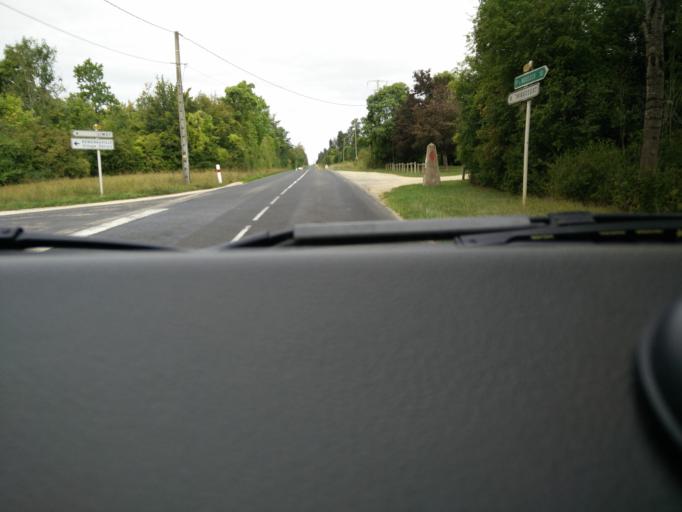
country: FR
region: Lorraine
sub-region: Departement de Meurthe-et-Moselle
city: Montauville
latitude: 48.9102
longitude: 5.9281
